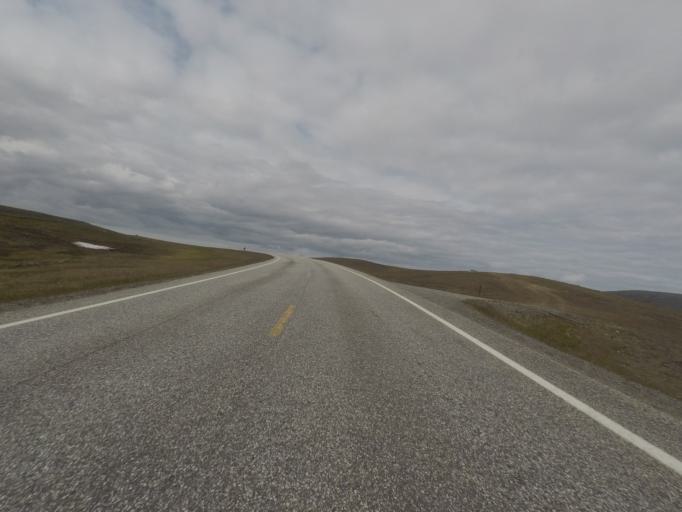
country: NO
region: Finnmark Fylke
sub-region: Nordkapp
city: Honningsvag
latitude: 71.0342
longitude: 25.8343
